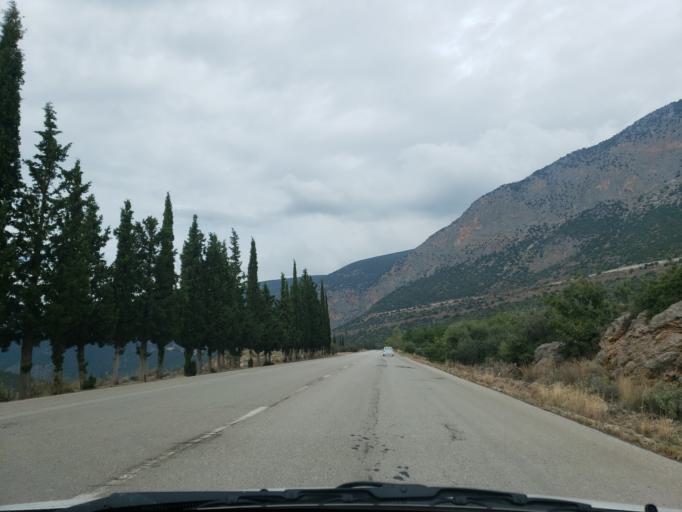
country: GR
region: Central Greece
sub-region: Nomos Fokidos
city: Delphi
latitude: 38.4824
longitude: 22.4613
